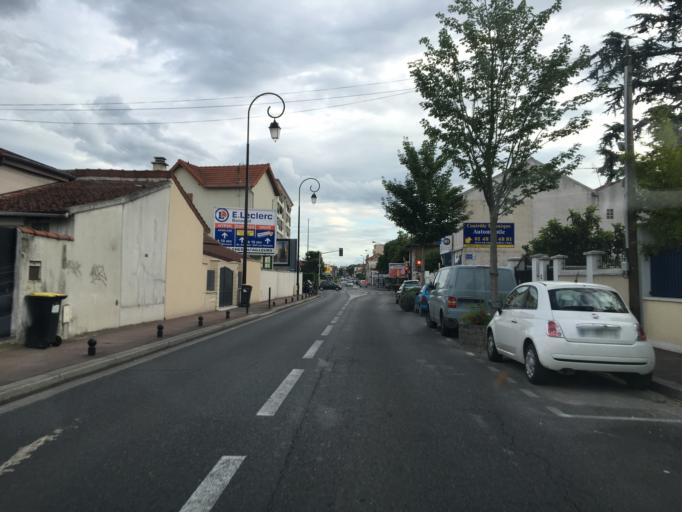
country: FR
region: Ile-de-France
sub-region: Departement du Val-de-Marne
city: Saint-Maur-des-Fosses
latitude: 48.7941
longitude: 2.4984
